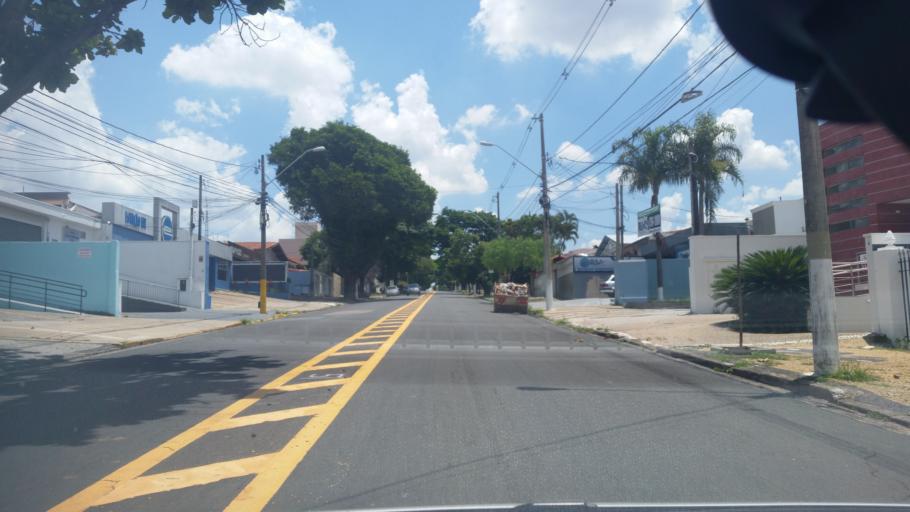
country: BR
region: Sao Paulo
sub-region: Campinas
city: Campinas
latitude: -22.8779
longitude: -47.0529
